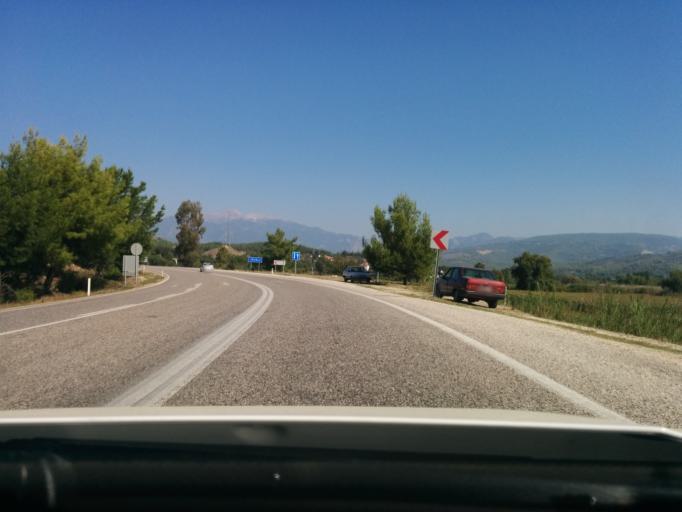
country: TR
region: Mugla
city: Kemer
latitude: 36.6254
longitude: 29.3575
